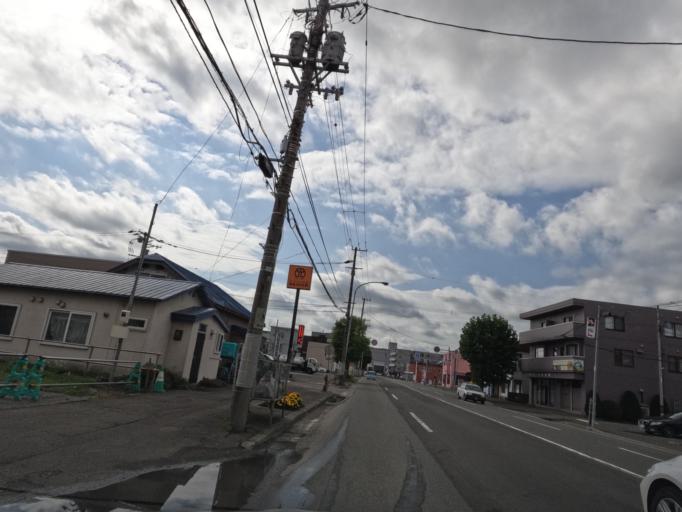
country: JP
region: Hokkaido
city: Chitose
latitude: 42.8193
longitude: 141.6532
